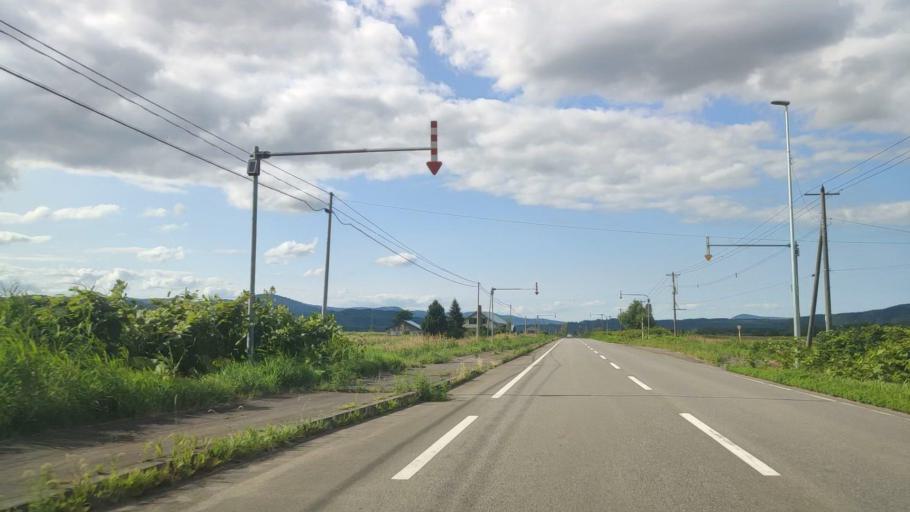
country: JP
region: Hokkaido
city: Nayoro
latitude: 44.5816
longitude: 142.3089
